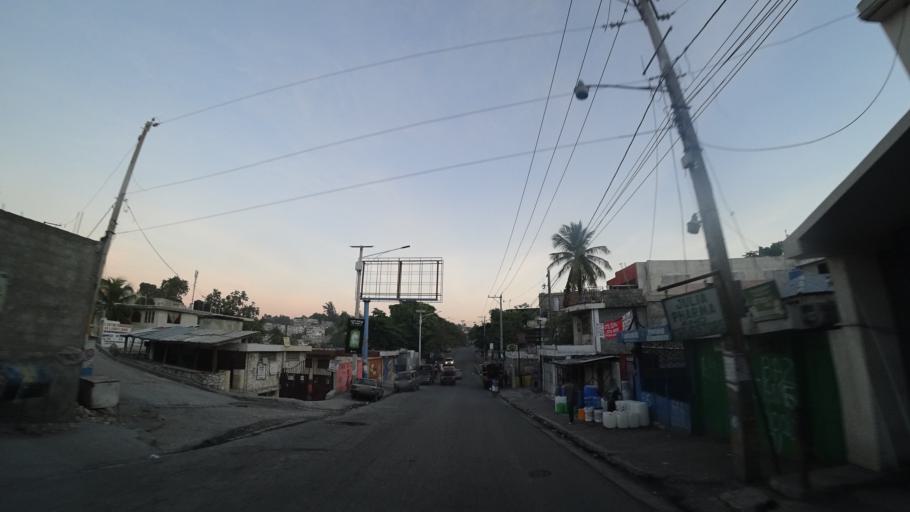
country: HT
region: Ouest
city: Delmas 73
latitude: 18.5466
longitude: -72.3173
